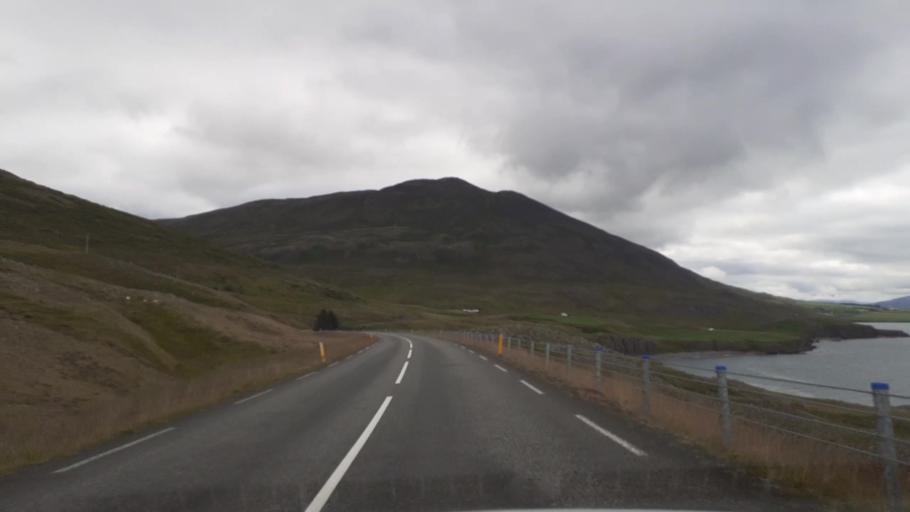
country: IS
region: Northeast
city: Akureyri
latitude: 65.8256
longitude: -18.0567
